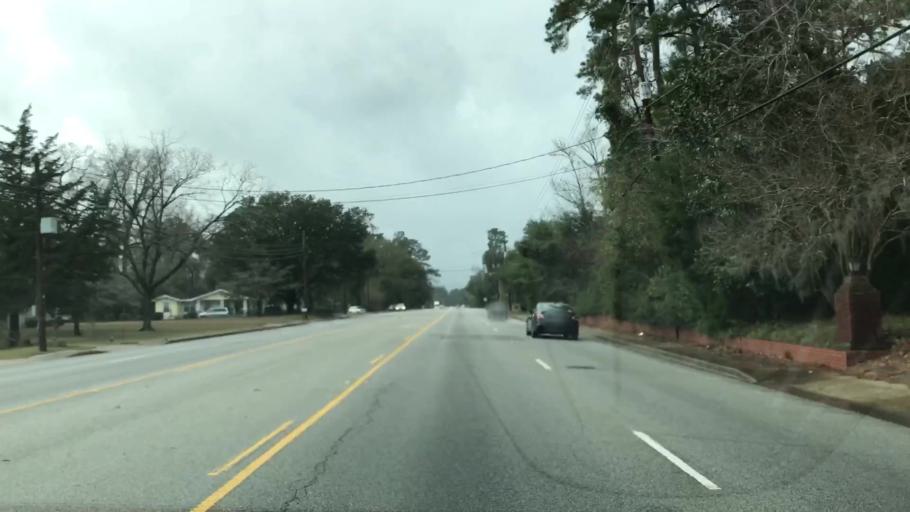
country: US
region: South Carolina
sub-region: Horry County
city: Conway
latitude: 33.8280
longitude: -79.0646
